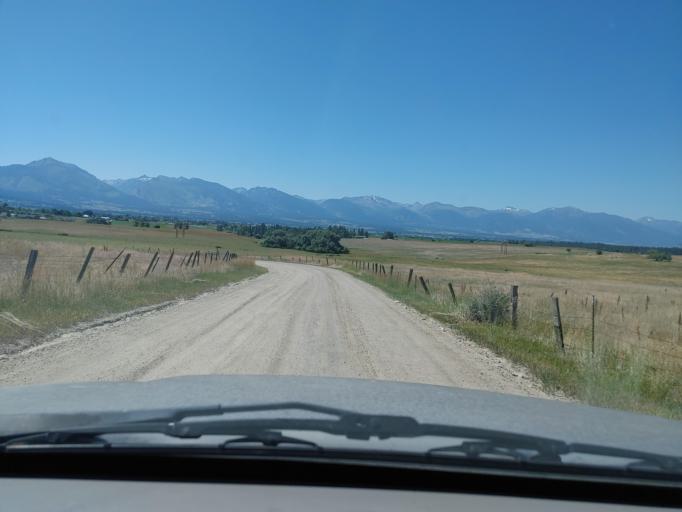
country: US
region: Montana
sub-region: Ravalli County
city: Hamilton
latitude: 46.2769
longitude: -114.0248
